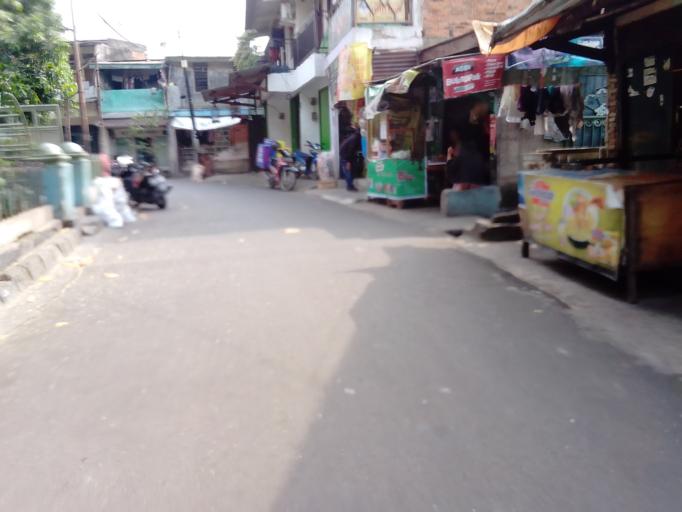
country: ID
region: Jakarta Raya
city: Jakarta
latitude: -6.1974
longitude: 106.8082
